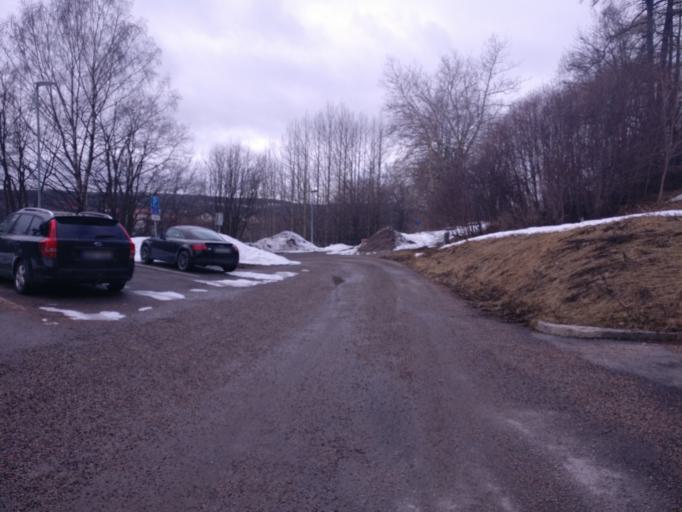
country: SE
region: Vaesternorrland
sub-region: Sundsvalls Kommun
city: Sundsvall
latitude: 62.3955
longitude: 17.2922
